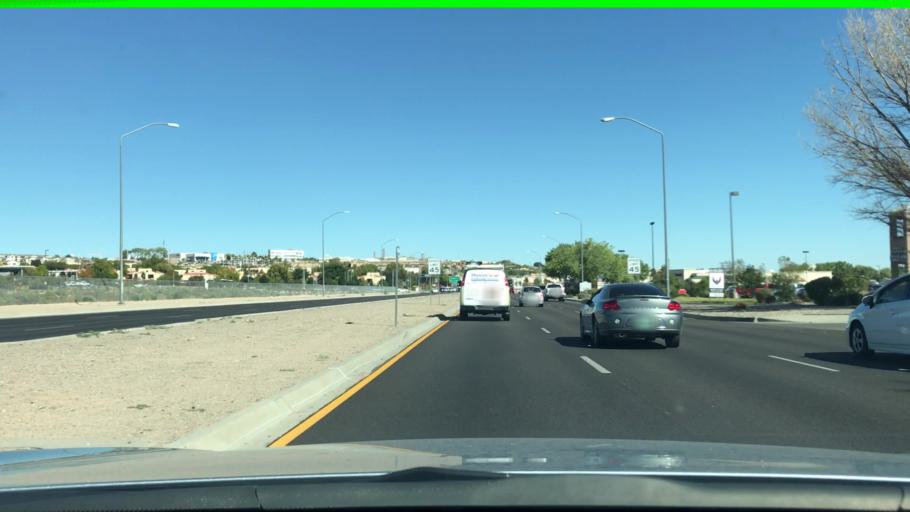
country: US
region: New Mexico
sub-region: Sandoval County
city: Rio Rancho
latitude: 35.2027
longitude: -106.6598
